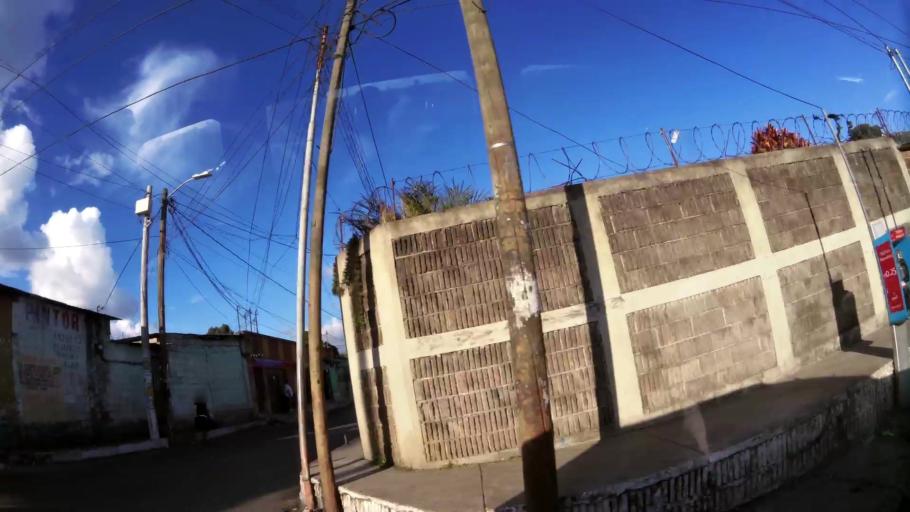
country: GT
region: Guatemala
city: Villa Nueva
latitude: 14.5217
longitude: -90.5876
